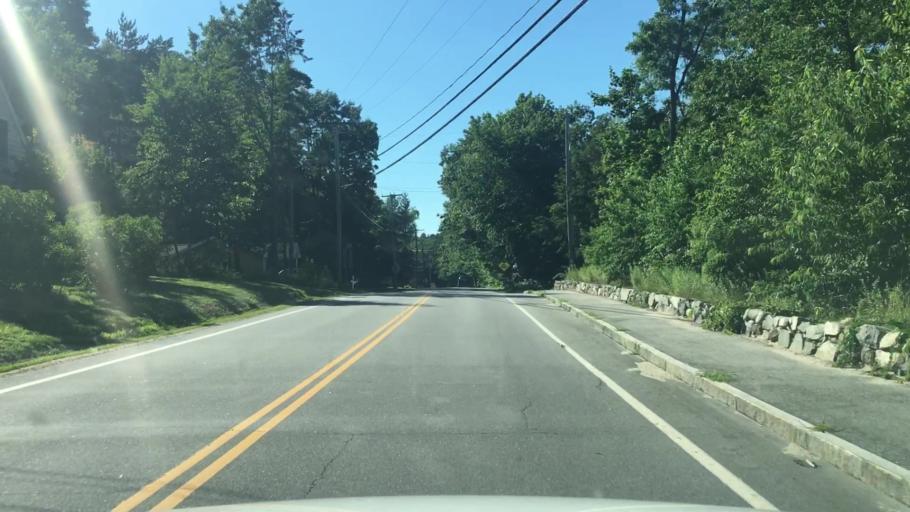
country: US
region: New Hampshire
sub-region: Rockingham County
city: Newmarket
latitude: 43.0363
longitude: -70.9460
